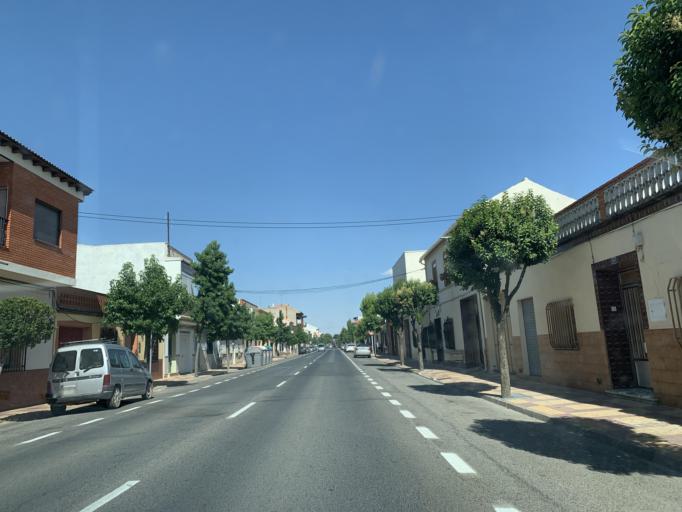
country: ES
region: Castille-La Mancha
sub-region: Provincia de Ciudad Real
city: Argamasilla de Alba
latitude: 39.1286
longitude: -3.0988
